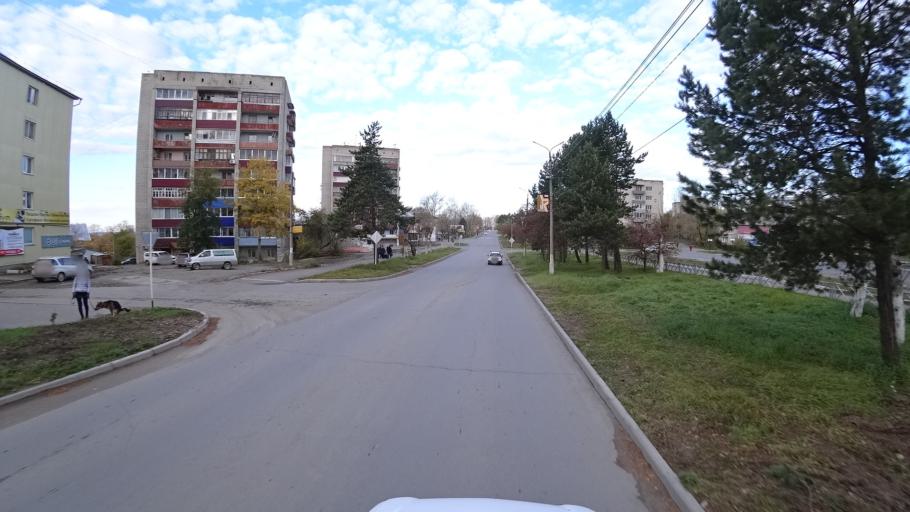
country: RU
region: Khabarovsk Krai
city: Amursk
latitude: 50.2283
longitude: 136.9065
